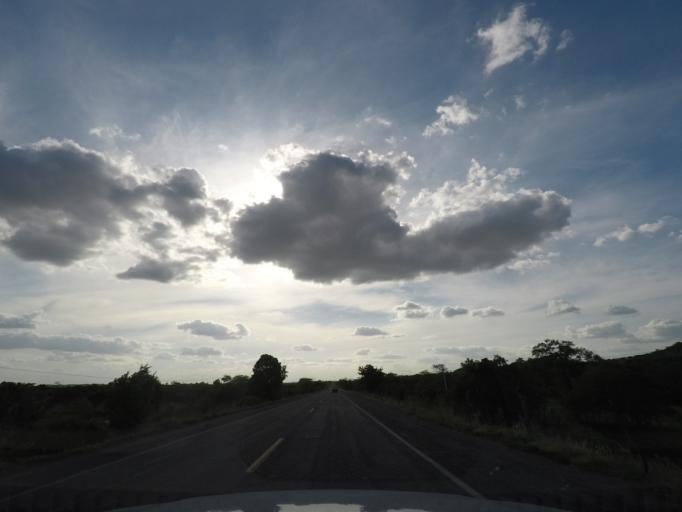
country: BR
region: Bahia
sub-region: Anguera
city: Anguera
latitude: -12.1848
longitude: -39.4759
